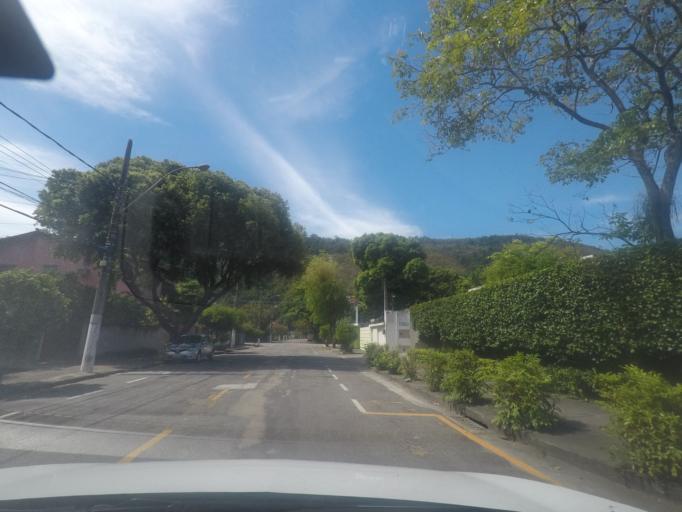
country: BR
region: Rio de Janeiro
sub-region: Niteroi
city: Niteroi
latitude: -22.9162
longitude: -43.0898
